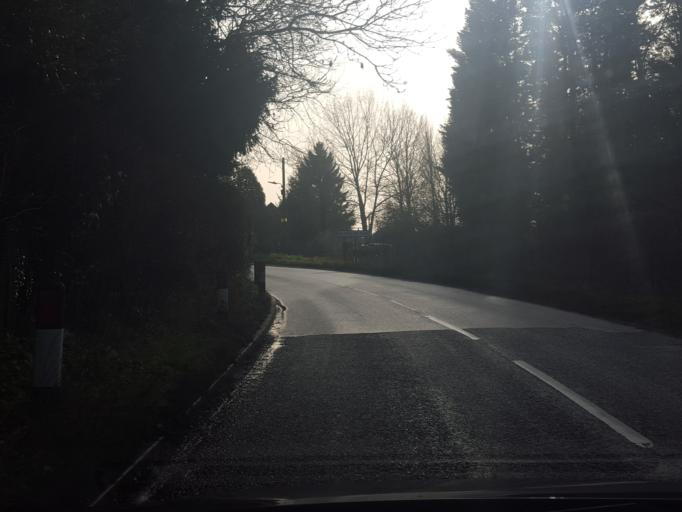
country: GB
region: England
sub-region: Suffolk
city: Sudbury
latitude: 51.9765
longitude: 0.7755
